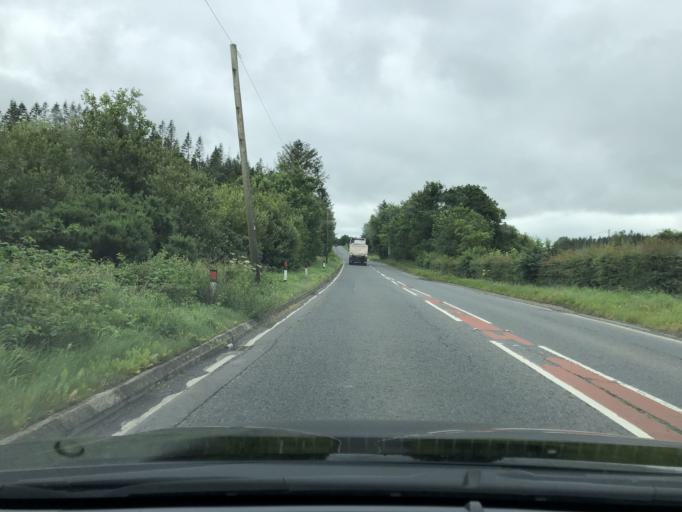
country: GB
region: Northern Ireland
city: Ballynahinch
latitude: 54.3509
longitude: -5.8515
